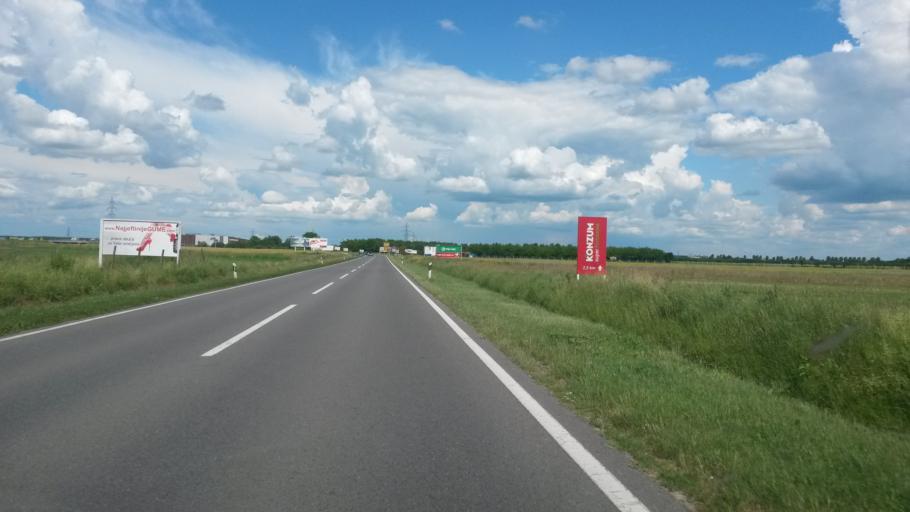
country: HR
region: Osjecko-Baranjska
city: Visnjevac
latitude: 45.5486
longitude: 18.6223
